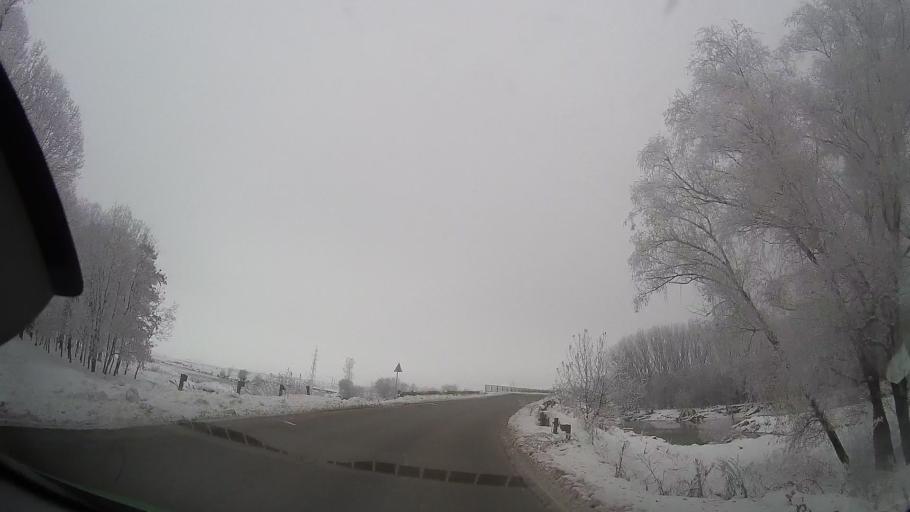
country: RO
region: Neamt
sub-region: Comuna Horia
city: Cotu Vames
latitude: 46.8815
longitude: 26.9718
